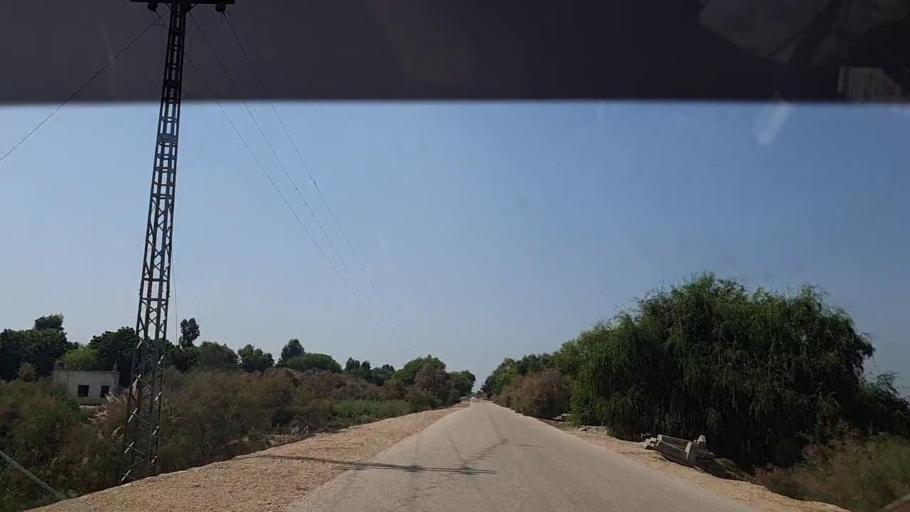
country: PK
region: Sindh
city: Ghauspur
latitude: 28.1555
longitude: 69.1553
